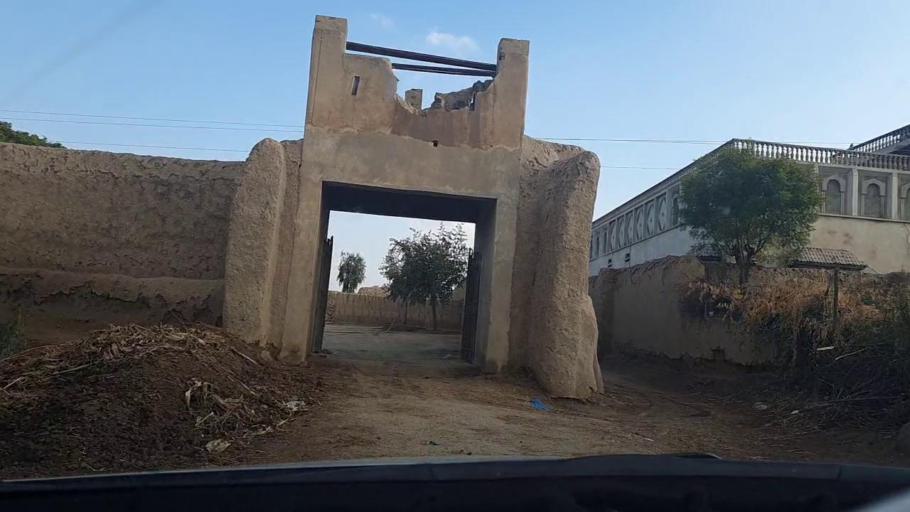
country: PK
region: Sindh
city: Tando Mittha Khan
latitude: 25.9160
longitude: 69.3048
